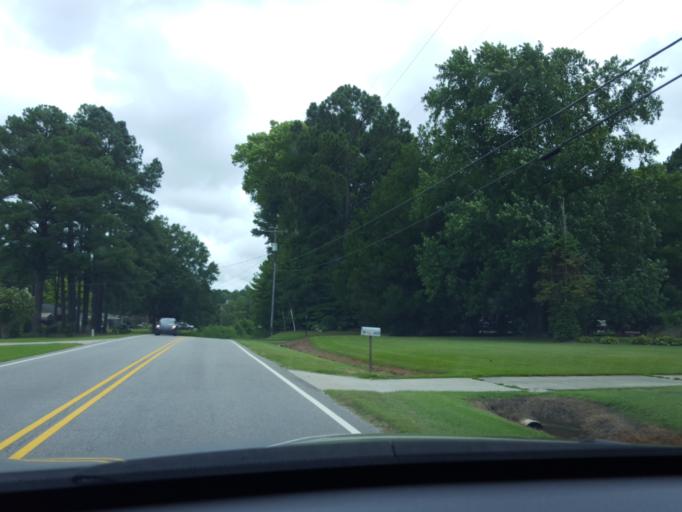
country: US
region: North Carolina
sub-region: Martin County
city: Williamston
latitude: 35.7976
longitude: -76.9020
